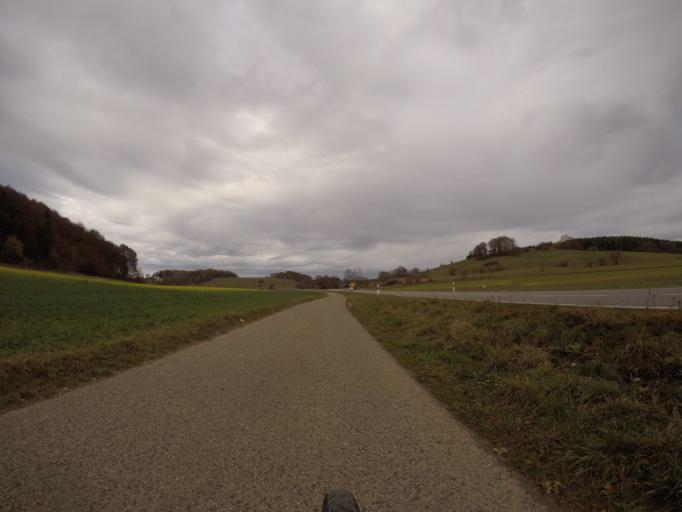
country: DE
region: Baden-Wuerttemberg
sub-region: Tuebingen Region
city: Sankt Johann
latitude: 48.4154
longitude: 9.2865
